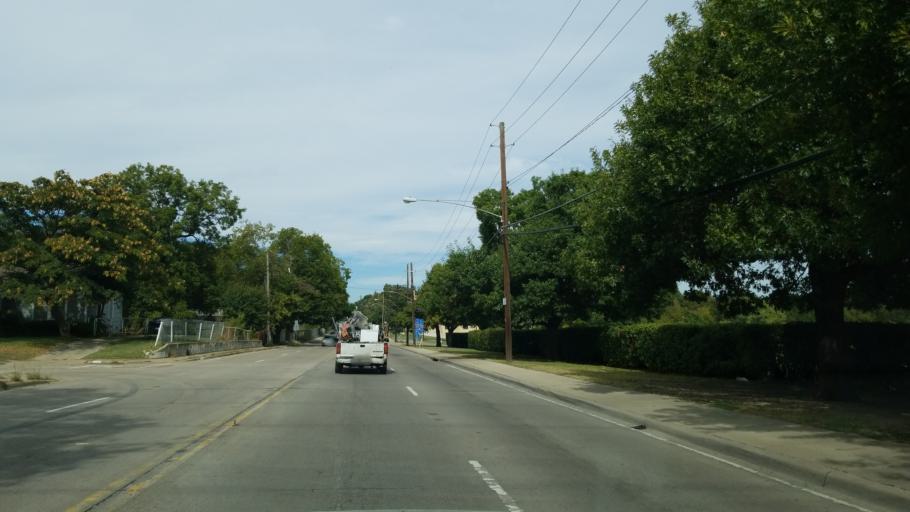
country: US
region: Texas
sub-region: Dallas County
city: Dallas
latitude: 32.7852
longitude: -96.7374
